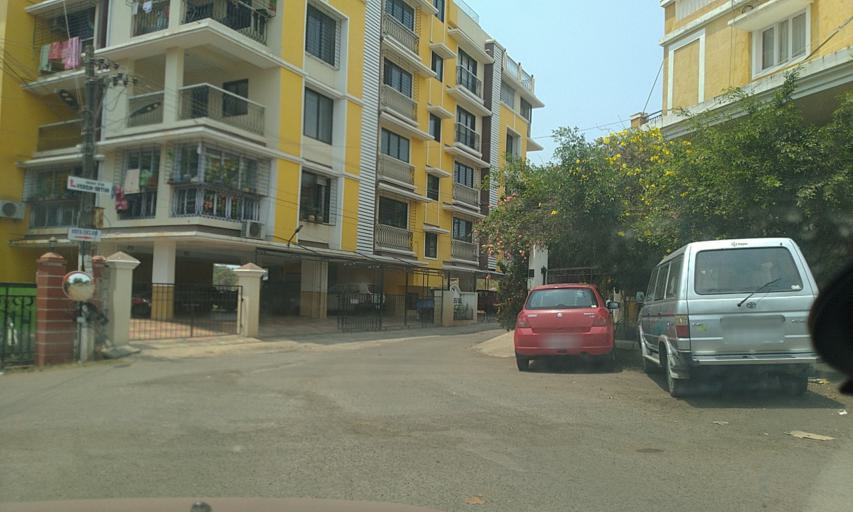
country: IN
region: Goa
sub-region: North Goa
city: Panaji
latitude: 15.5214
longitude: 73.8210
